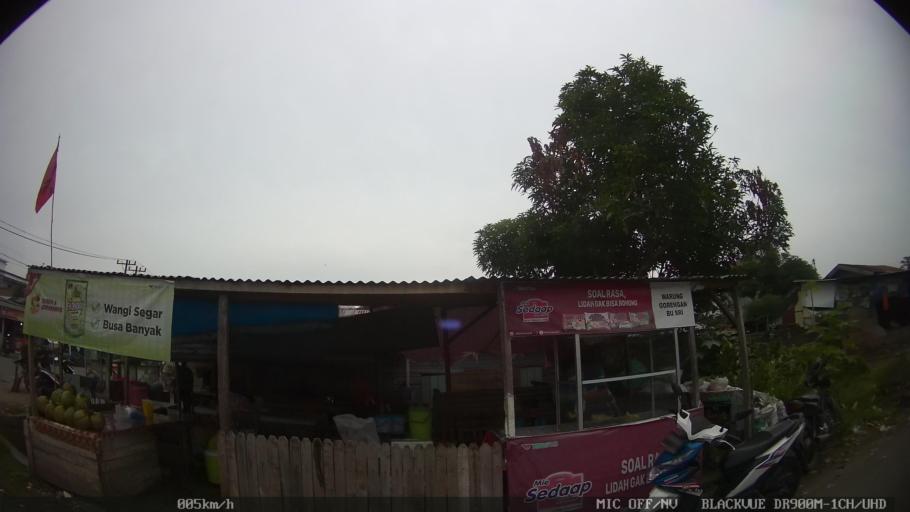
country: ID
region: North Sumatra
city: Deli Tua
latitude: 3.5371
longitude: 98.7321
